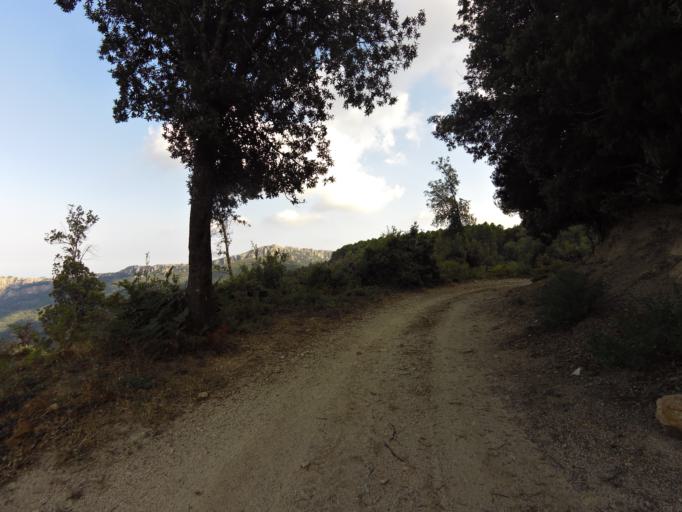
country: IT
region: Calabria
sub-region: Provincia di Reggio Calabria
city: Pazzano
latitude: 38.4772
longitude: 16.4062
